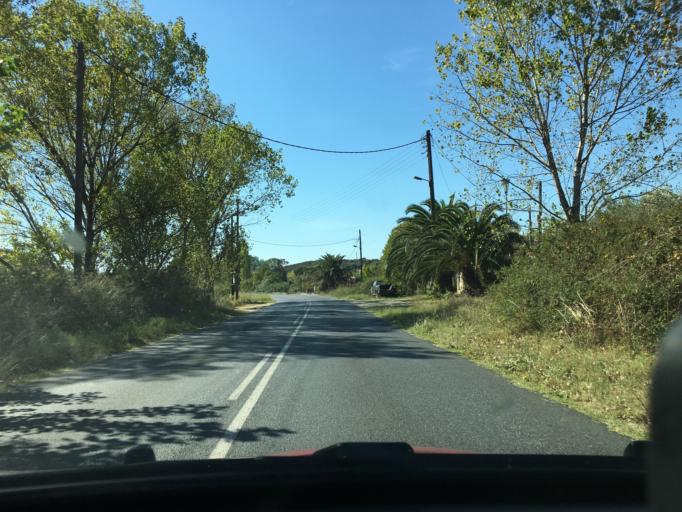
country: GR
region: Central Macedonia
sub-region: Nomos Chalkidikis
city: Nea Roda
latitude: 40.3694
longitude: 23.9188
